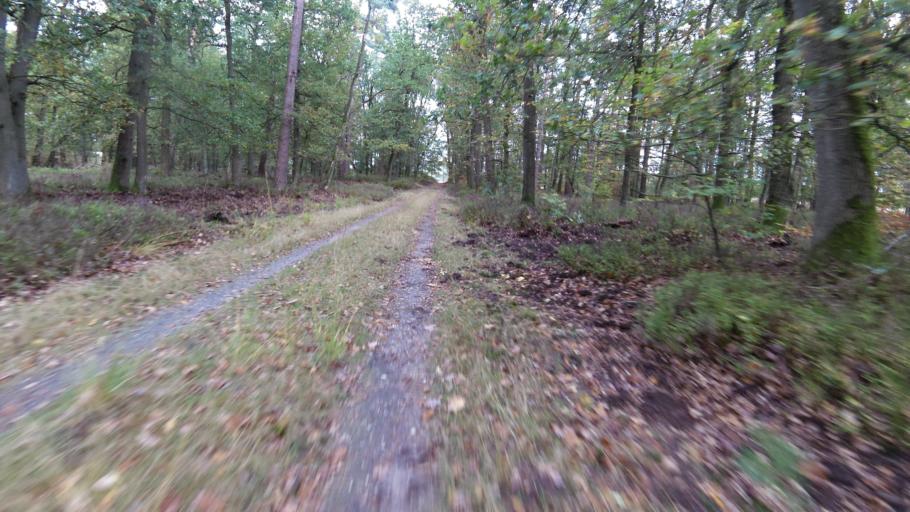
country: NL
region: Gelderland
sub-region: Gemeente Epe
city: Emst
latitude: 52.3212
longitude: 5.8821
